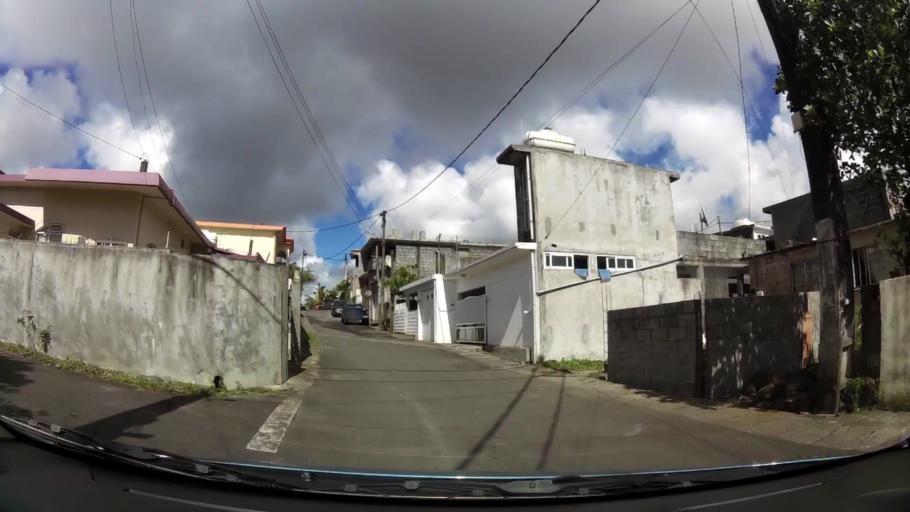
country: MU
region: Plaines Wilhems
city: Curepipe
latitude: -20.3334
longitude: 57.5257
